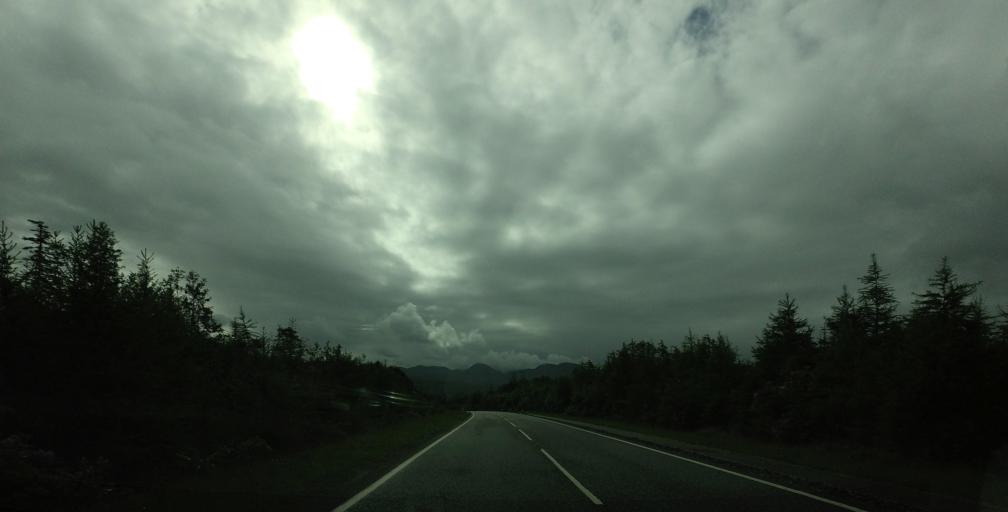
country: GB
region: Scotland
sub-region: Argyll and Bute
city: Isle Of Mull
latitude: 56.8999
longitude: -5.8022
